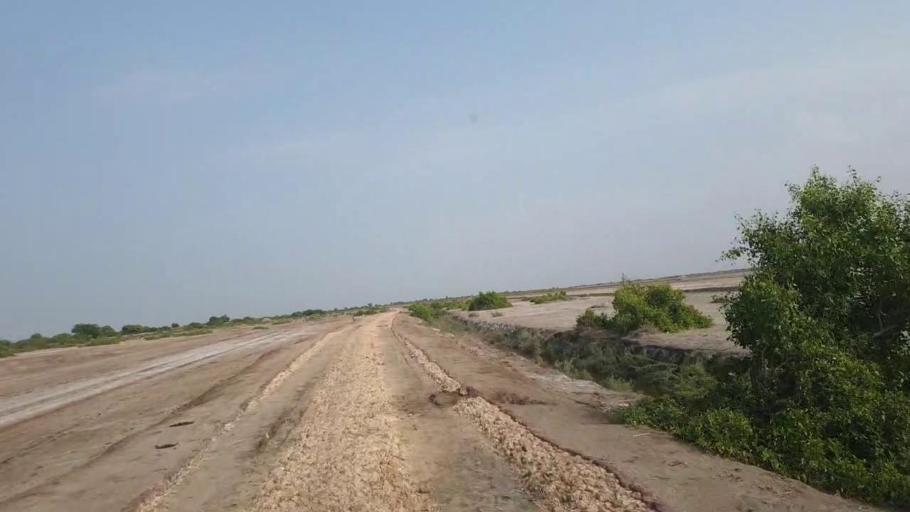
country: PK
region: Sindh
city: Kadhan
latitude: 24.4443
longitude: 68.8115
